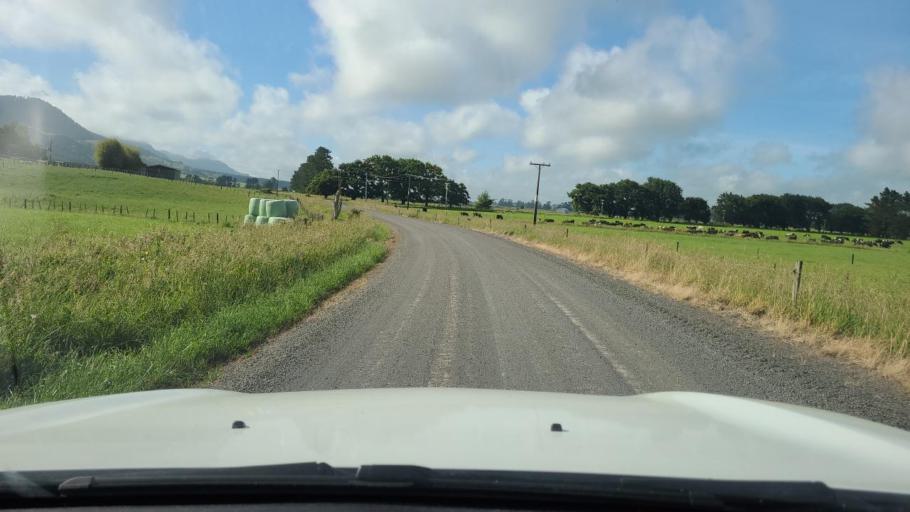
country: NZ
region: Bay of Plenty
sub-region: Western Bay of Plenty District
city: Katikati
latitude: -37.6138
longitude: 175.7955
